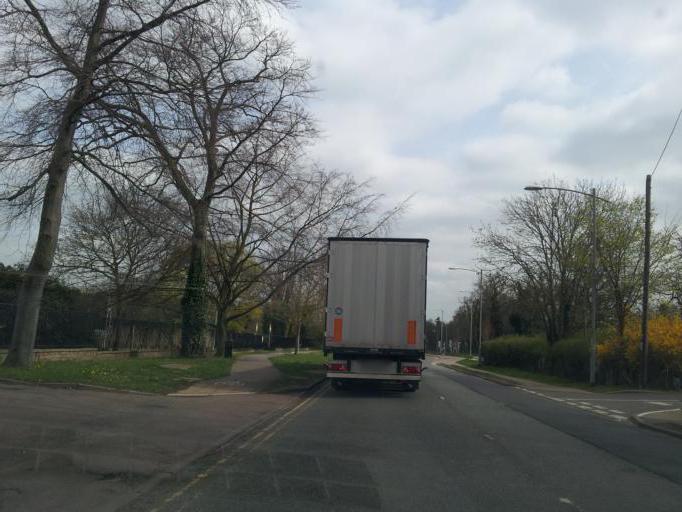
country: GB
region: England
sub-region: Cambridgeshire
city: Cambridge
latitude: 52.1804
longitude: 0.1197
